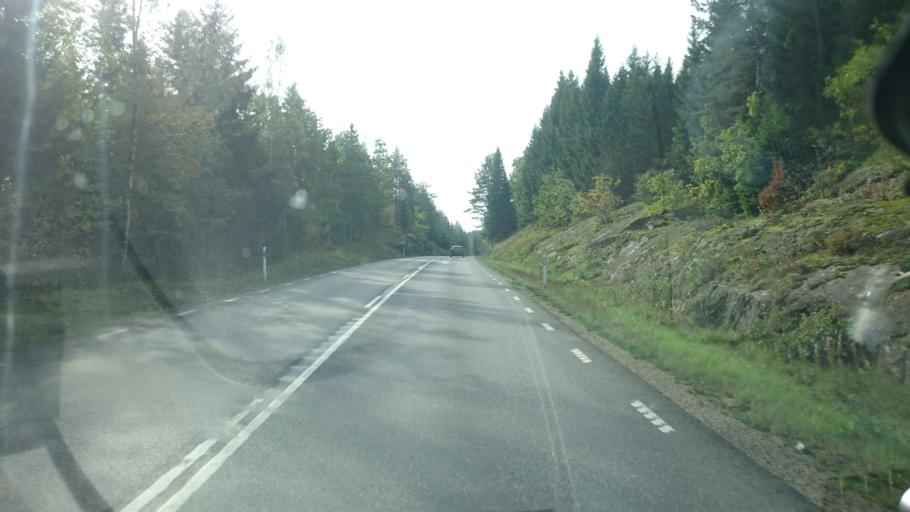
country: SE
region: Vaestra Goetaland
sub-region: Alingsas Kommun
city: Sollebrunn
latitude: 58.0364
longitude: 12.4658
